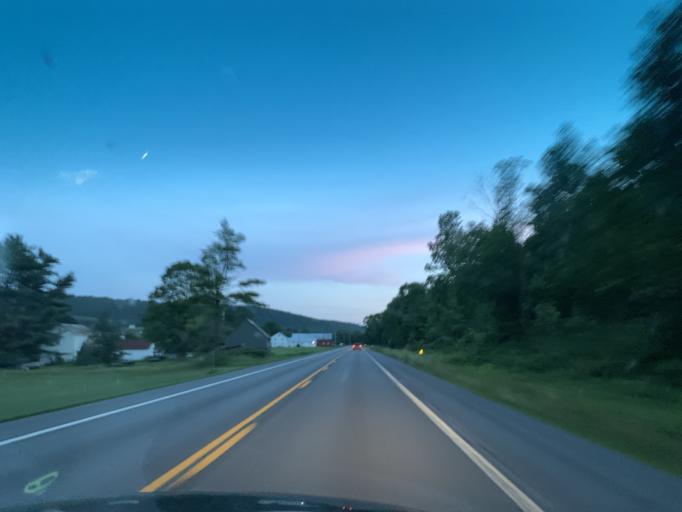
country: US
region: New York
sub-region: Chenango County
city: New Berlin
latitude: 42.5711
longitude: -75.3400
